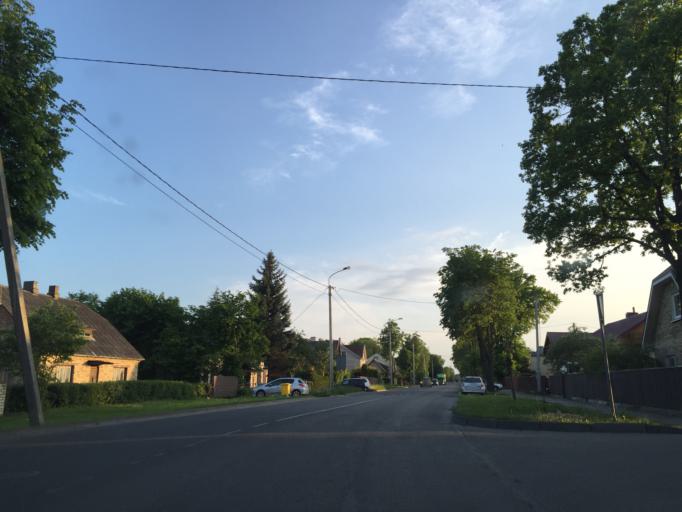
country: LT
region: Siauliu apskritis
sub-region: Siauliai
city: Siauliai
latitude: 55.9422
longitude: 23.3081
